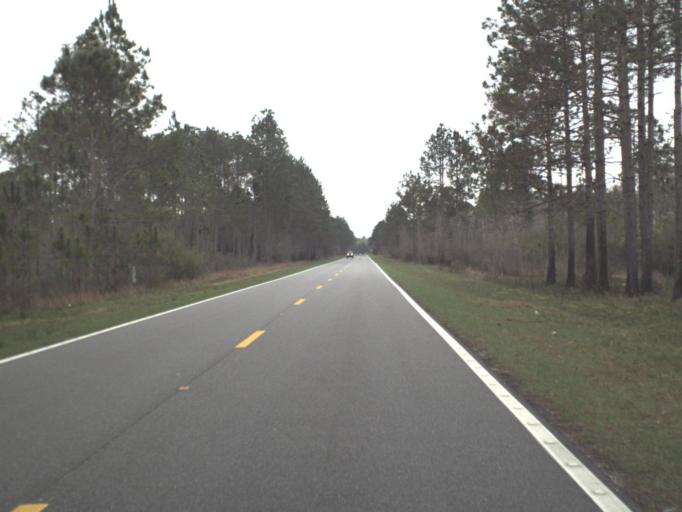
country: US
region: Florida
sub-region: Gulf County
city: Wewahitchka
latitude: 30.0418
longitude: -84.9835
